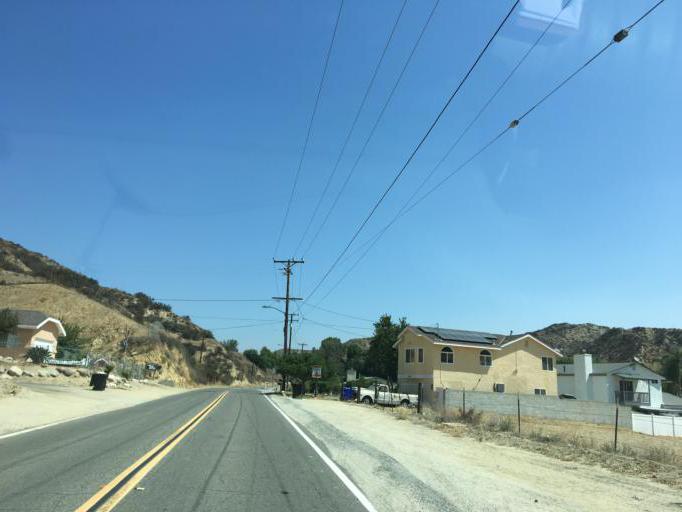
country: US
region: California
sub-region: Los Angeles County
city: Val Verde
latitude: 34.4379
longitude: -118.6584
